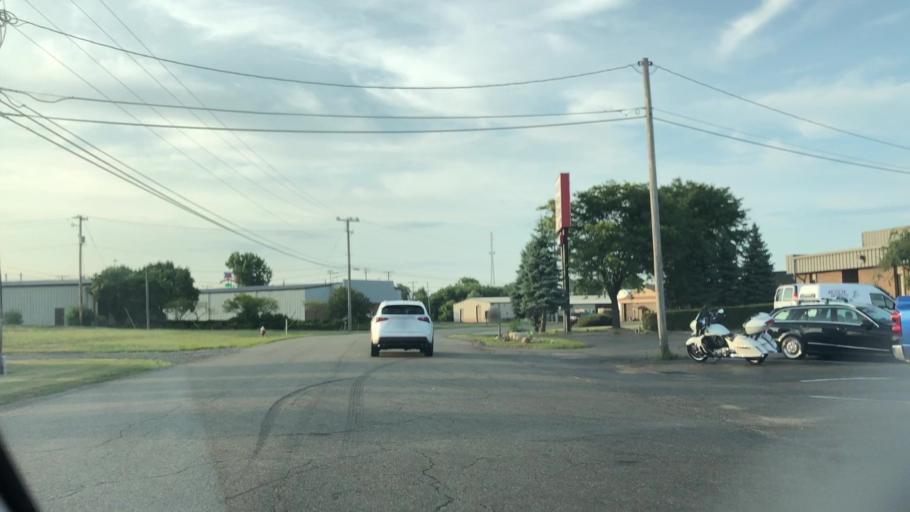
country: US
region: Ohio
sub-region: Stark County
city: North Canton
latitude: 40.8748
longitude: -81.4286
